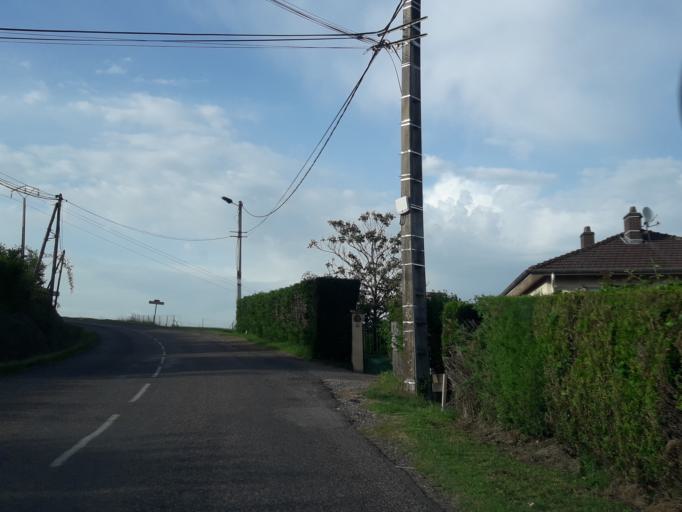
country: FR
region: Rhone-Alpes
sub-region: Departement du Rhone
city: Bessenay
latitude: 45.7512
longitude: 4.5428
